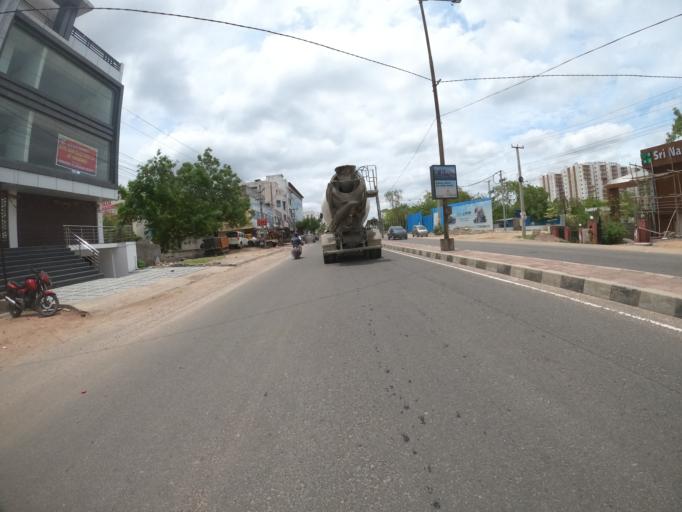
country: IN
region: Telangana
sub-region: Hyderabad
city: Hyderabad
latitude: 17.3848
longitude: 78.3596
